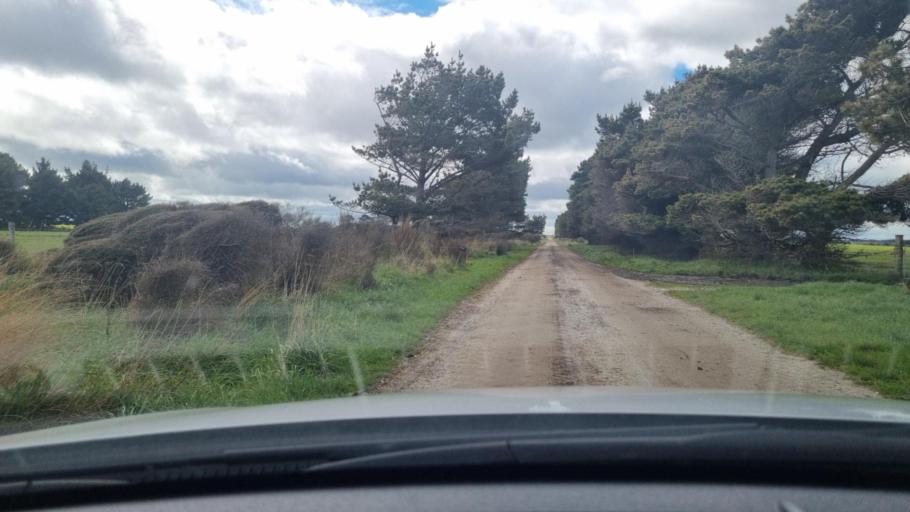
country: NZ
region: Southland
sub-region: Invercargill City
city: Bluff
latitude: -46.5709
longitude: 168.4989
